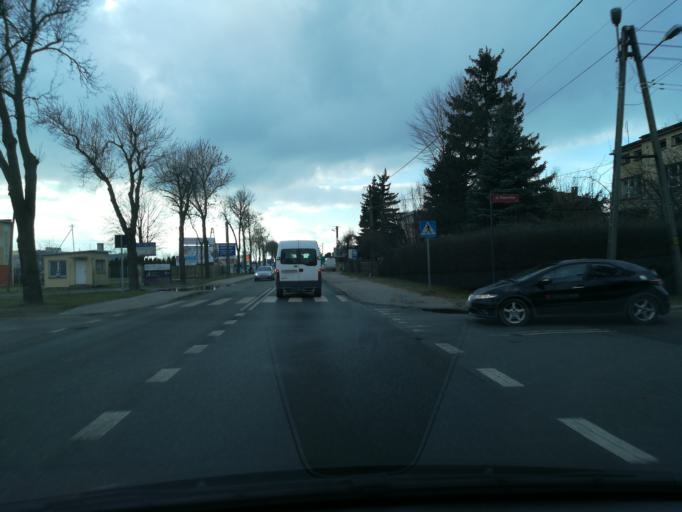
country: PL
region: Lodz Voivodeship
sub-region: Powiat radomszczanski
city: Radomsko
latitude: 51.0735
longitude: 19.4148
